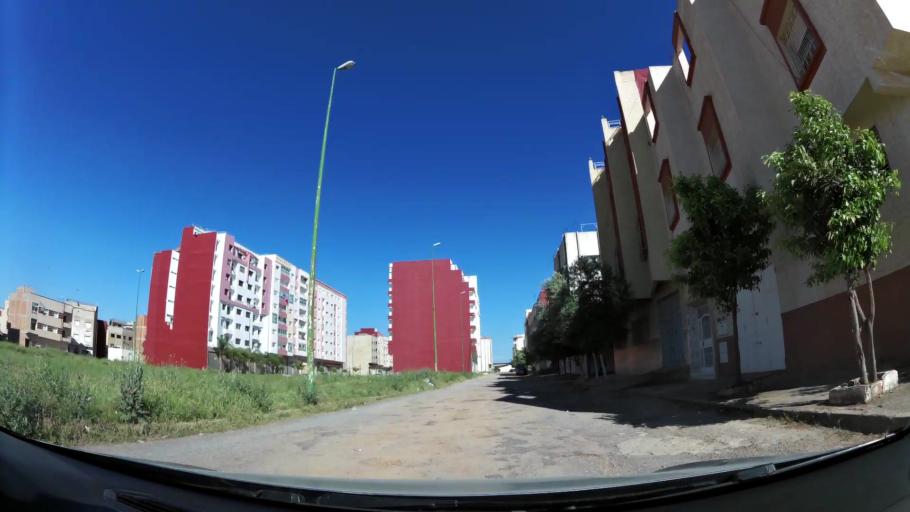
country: MA
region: Meknes-Tafilalet
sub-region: Meknes
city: Meknes
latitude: 33.8797
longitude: -5.5802
